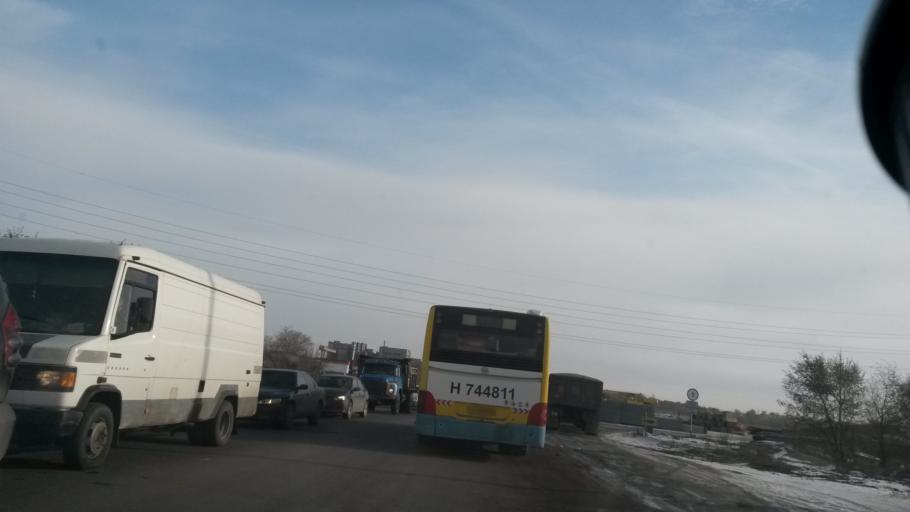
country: KZ
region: Qaraghandy
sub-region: Qaraghandy Qalasy
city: Karagandy
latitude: 49.8297
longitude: 73.0695
